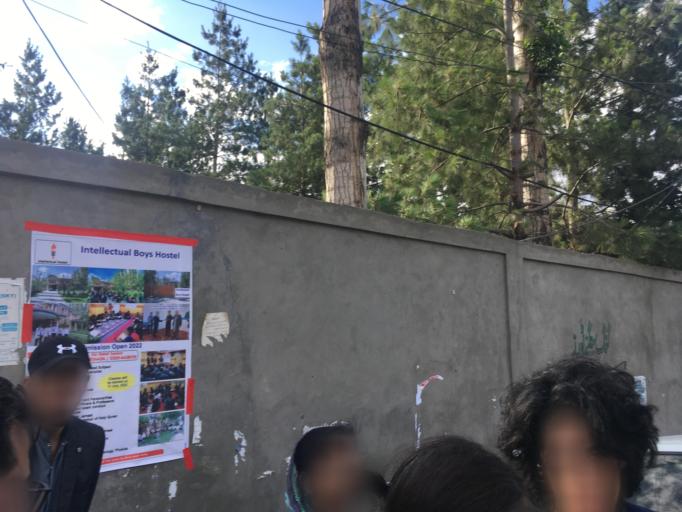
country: PK
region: Gilgit-Baltistan
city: Skardu
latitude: 35.2814
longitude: 75.6414
